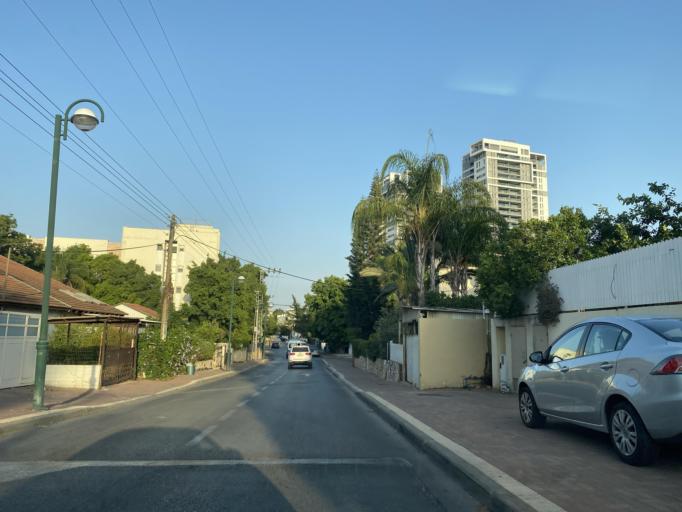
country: IL
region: Tel Aviv
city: Ramat HaSharon
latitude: 32.1343
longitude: 34.8570
